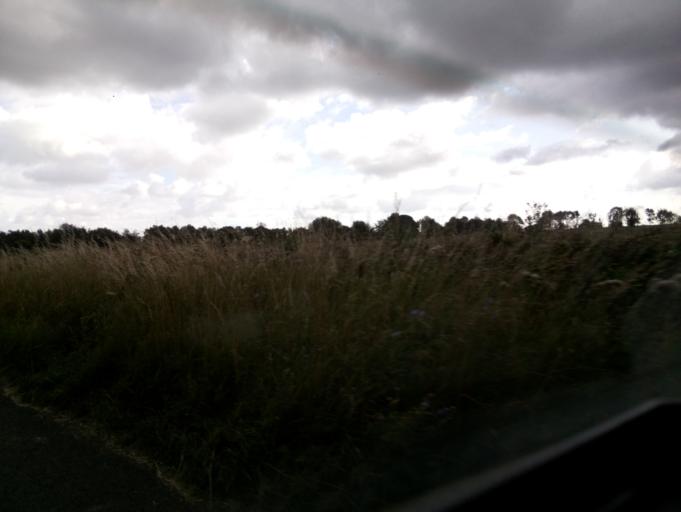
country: GB
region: England
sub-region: Gloucestershire
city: Chalford
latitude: 51.7785
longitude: -2.1016
